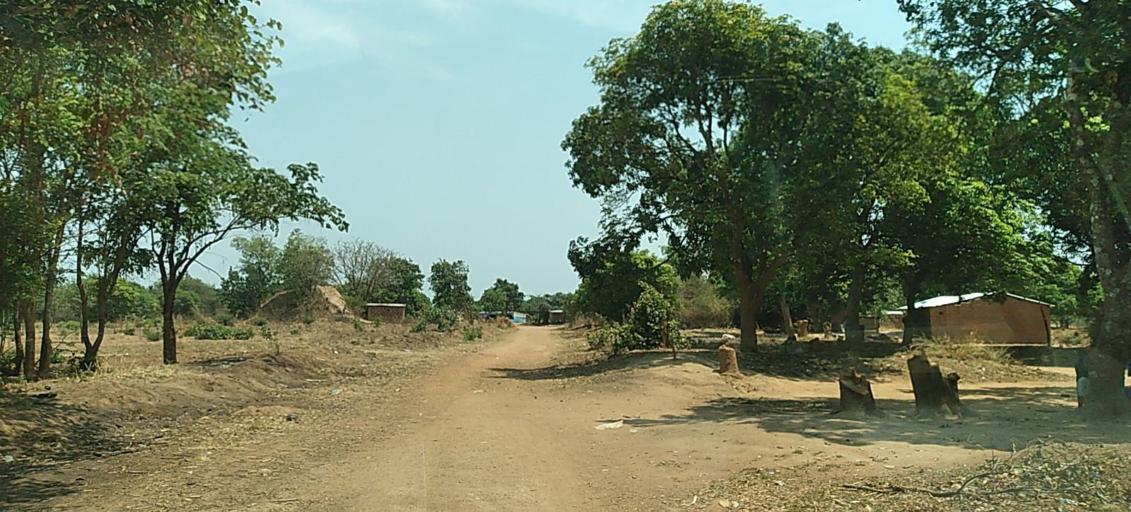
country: ZM
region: Copperbelt
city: Ndola
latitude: -13.0747
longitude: 28.7466
